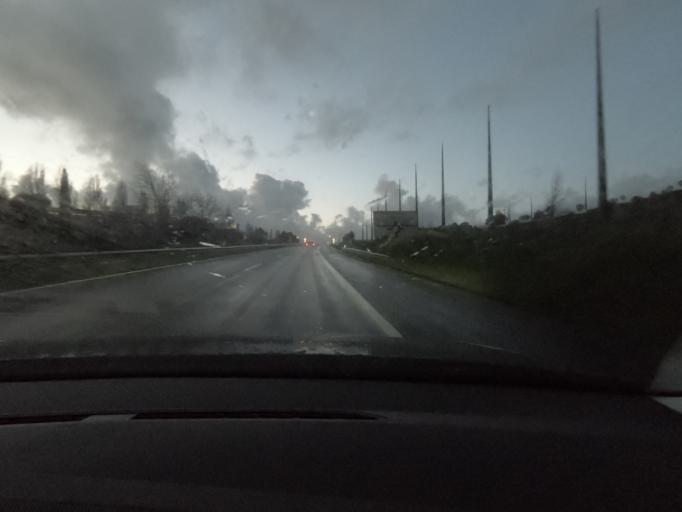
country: PT
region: Lisbon
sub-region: Sintra
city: Cacem
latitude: 38.7446
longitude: -9.3023
